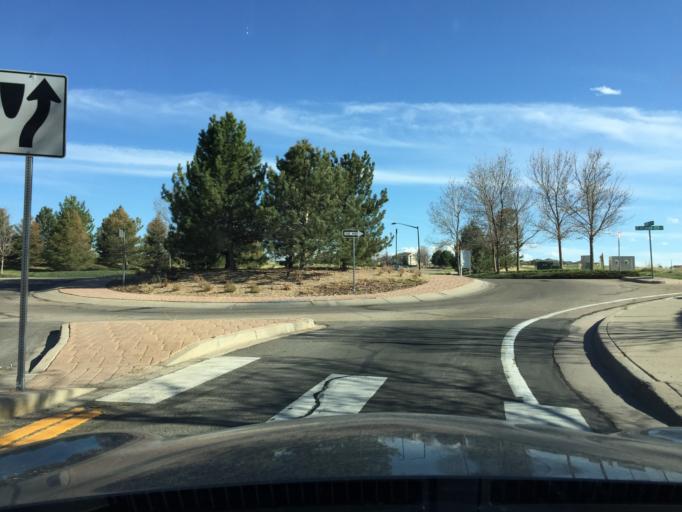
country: US
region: Colorado
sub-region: Boulder County
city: Erie
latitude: 40.0081
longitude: -105.0313
